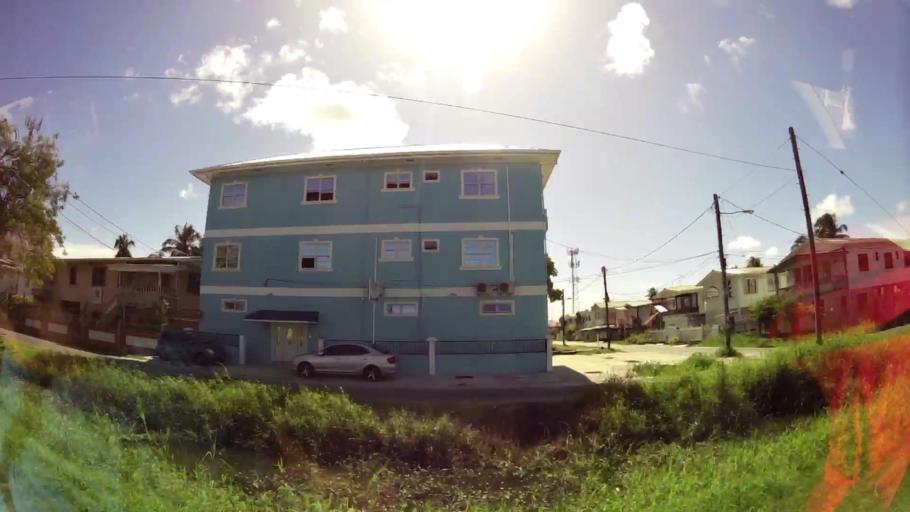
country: GY
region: Demerara-Mahaica
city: Georgetown
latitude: 6.8111
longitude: -58.1409
